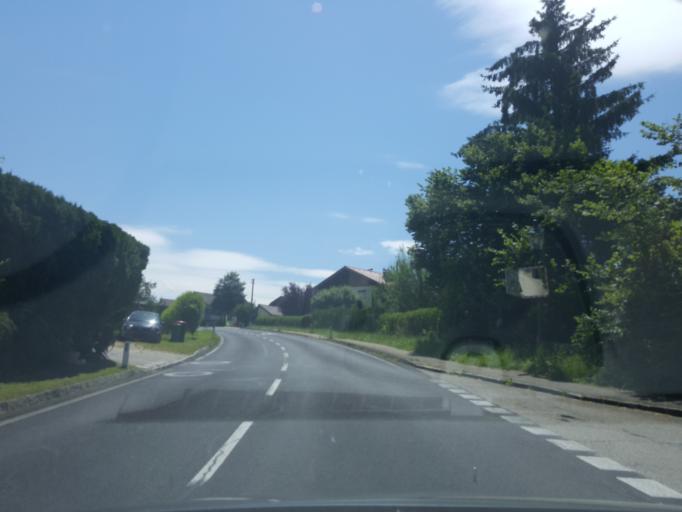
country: AT
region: Upper Austria
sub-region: Politischer Bezirk Vocklabruck
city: Seewalchen
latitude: 47.9630
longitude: 13.5714
